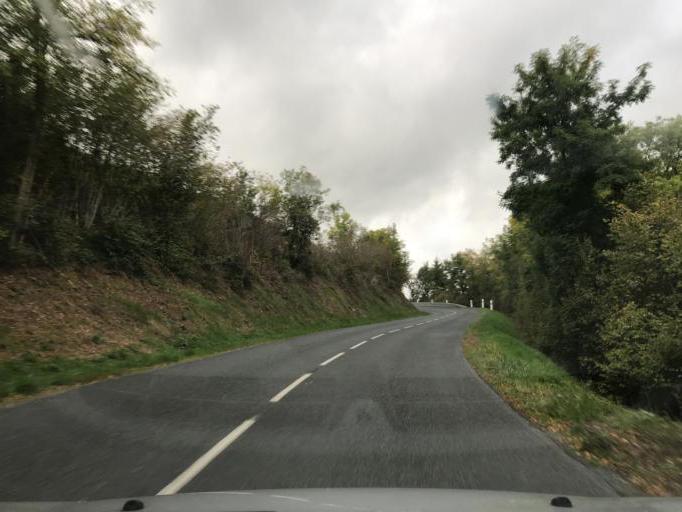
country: FR
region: Rhone-Alpes
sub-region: Departement du Rhone
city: Le Perreon
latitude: 46.0301
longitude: 4.5563
